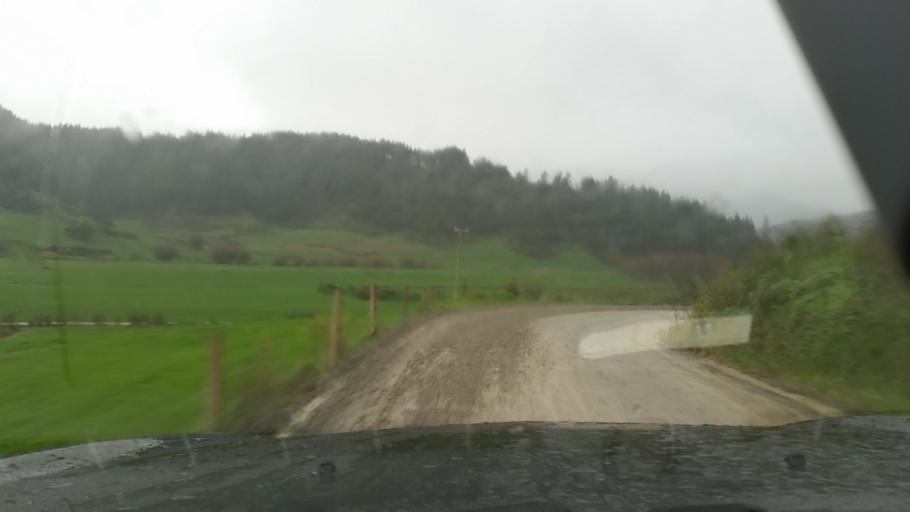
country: NZ
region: Marlborough
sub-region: Marlborough District
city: Picton
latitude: -41.3411
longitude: 173.9273
